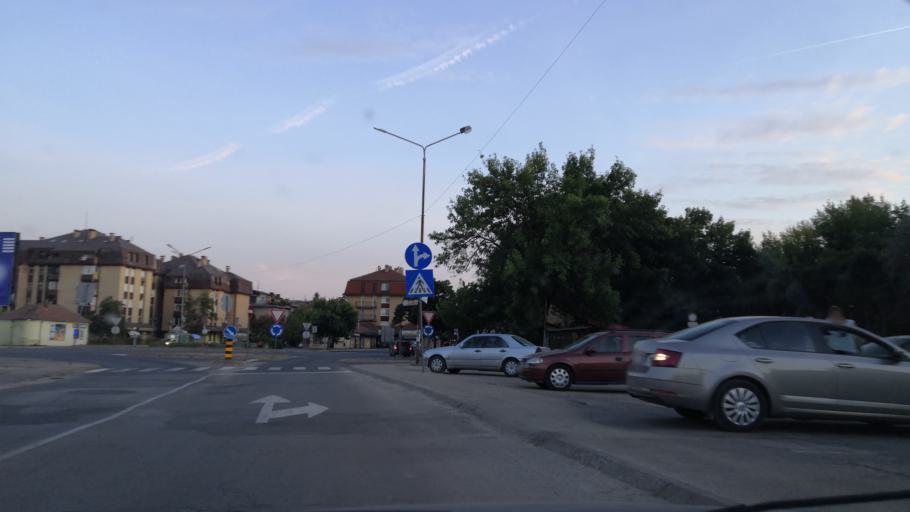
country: RS
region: Central Serbia
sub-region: Borski Okrug
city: Negotin
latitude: 44.2338
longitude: 22.5294
